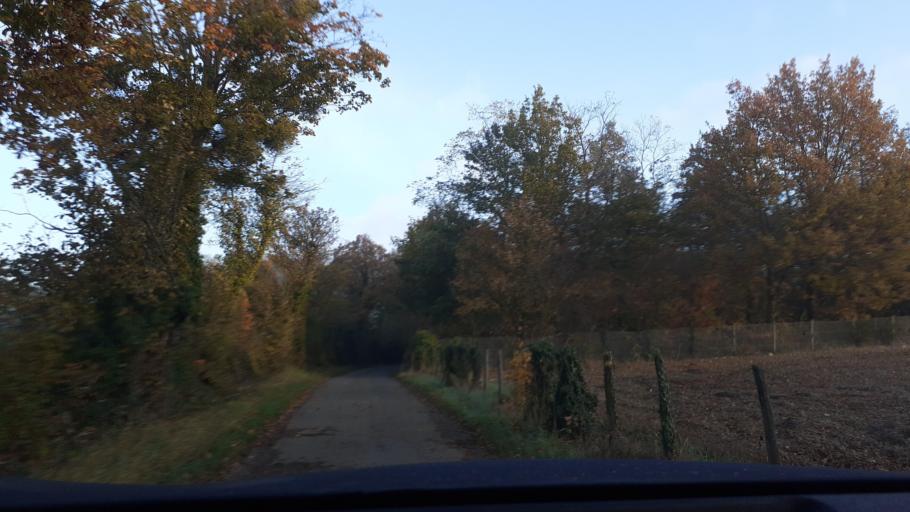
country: FR
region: Rhone-Alpes
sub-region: Departement du Rhone
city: Charnay
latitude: 45.9141
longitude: 4.6671
